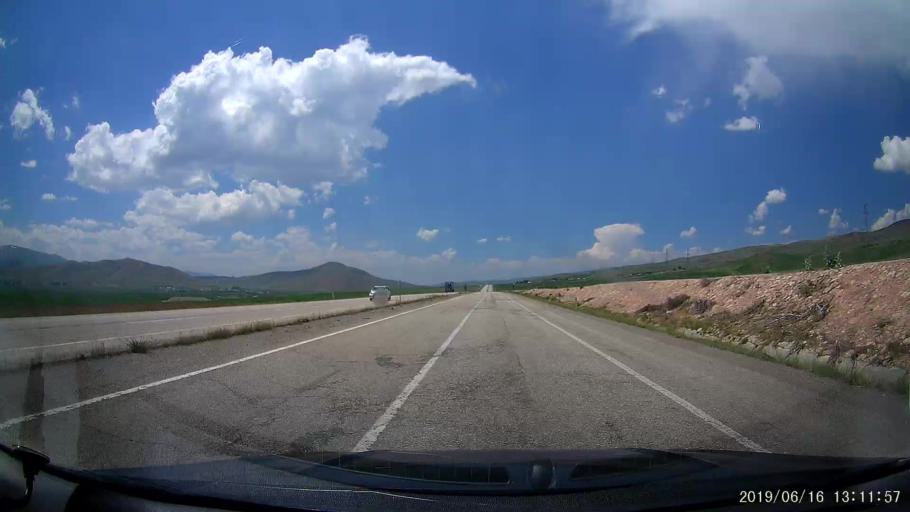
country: TR
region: Agri
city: Diyadin
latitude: 39.5955
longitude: 43.5926
